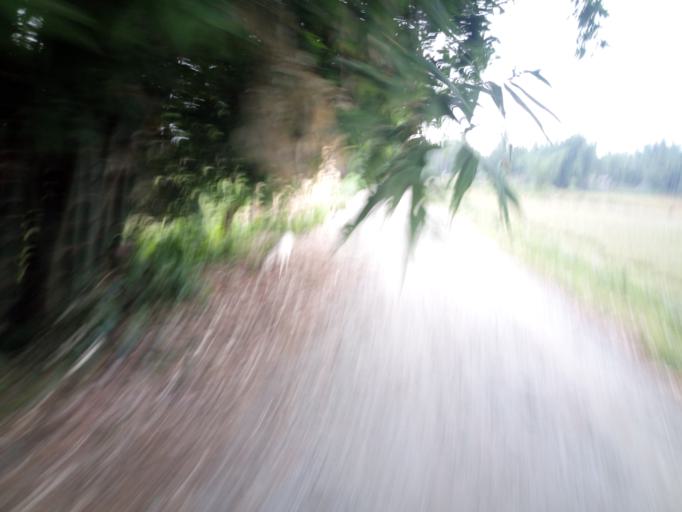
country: IN
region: Assam
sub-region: Darrang
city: Kharupatia
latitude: 26.6511
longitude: 92.2395
